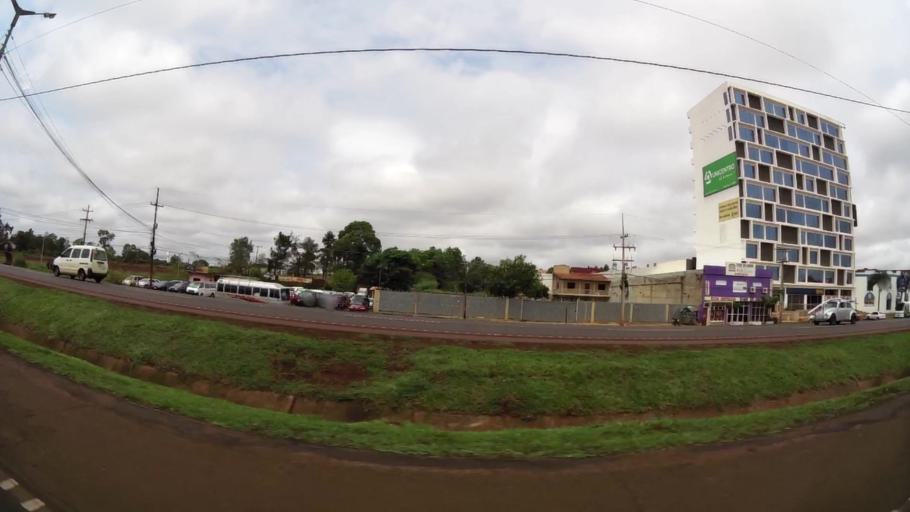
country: PY
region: Alto Parana
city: Ciudad del Este
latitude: -25.4964
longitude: -54.6781
